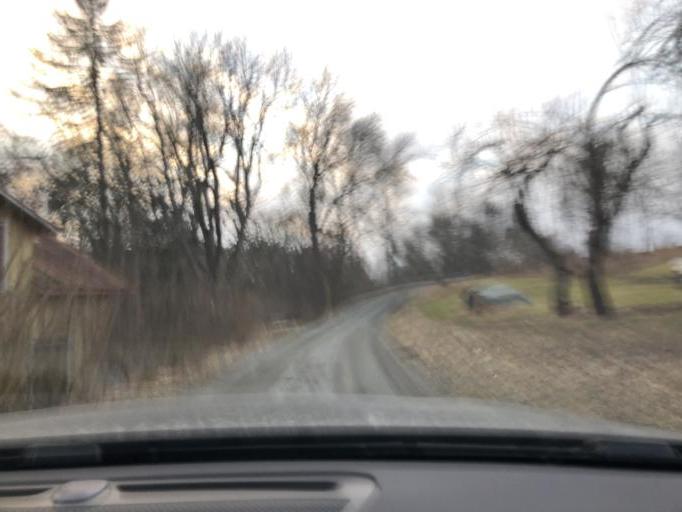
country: SE
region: Uppsala
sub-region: Uppsala Kommun
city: Gamla Uppsala
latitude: 59.9214
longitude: 17.6294
